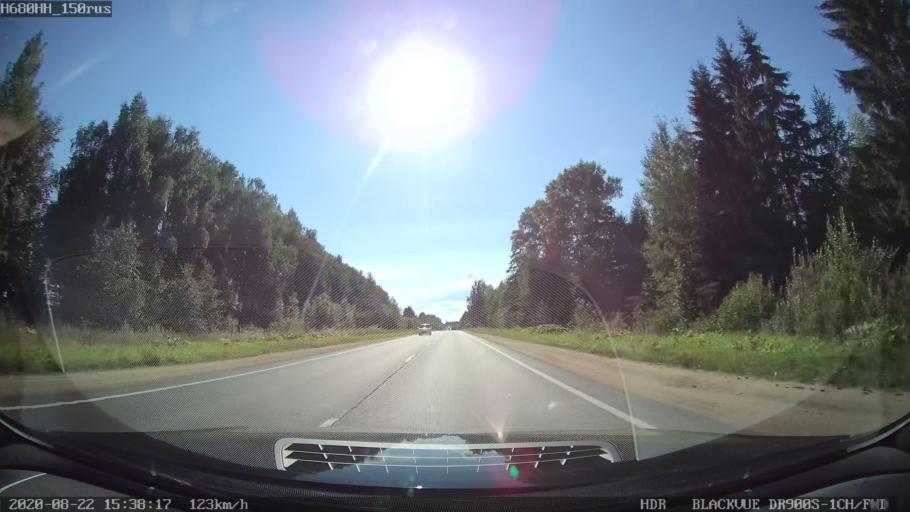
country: RU
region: Tverskaya
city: Bezhetsk
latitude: 57.7639
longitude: 36.6532
